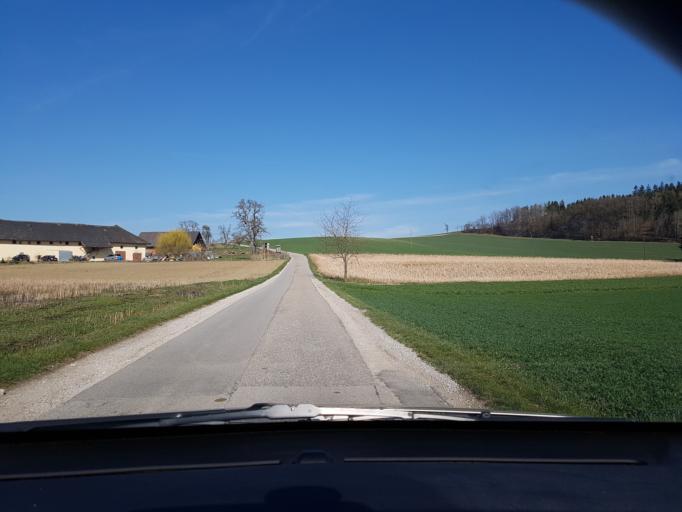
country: AT
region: Upper Austria
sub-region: Politischer Bezirk Linz-Land
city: Ansfelden
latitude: 48.1915
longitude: 14.3244
